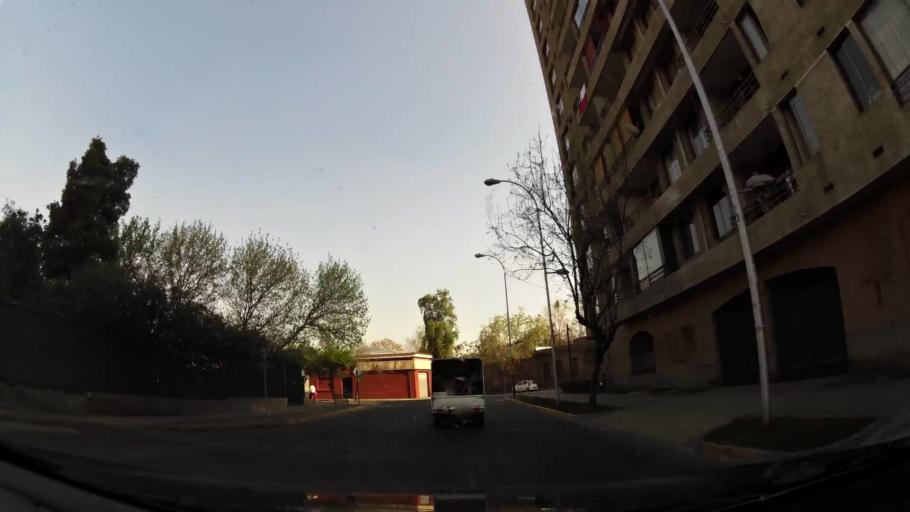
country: CL
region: Santiago Metropolitan
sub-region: Provincia de Santiago
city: Santiago
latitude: -33.4212
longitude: -70.6490
